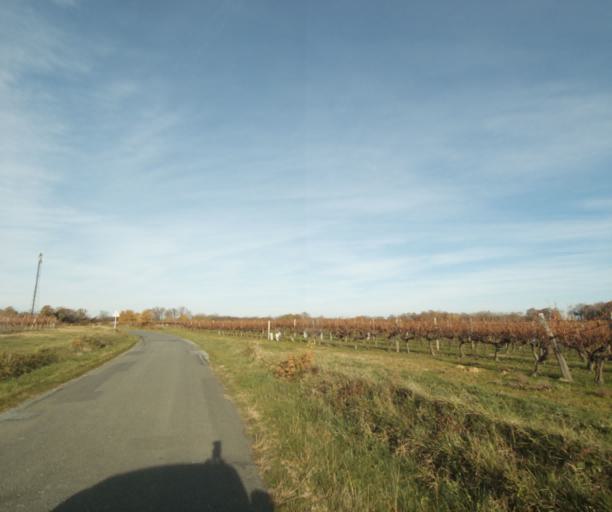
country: FR
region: Poitou-Charentes
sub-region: Departement de la Charente-Maritime
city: Chaniers
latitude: 45.7416
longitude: -0.5207
